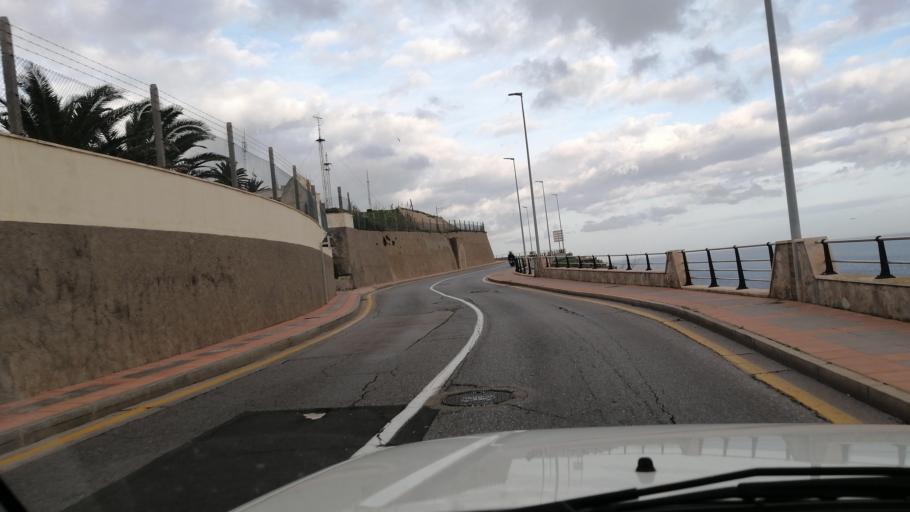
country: ES
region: Ceuta
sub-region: Ceuta
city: Ceuta
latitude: 35.8855
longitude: -5.3064
